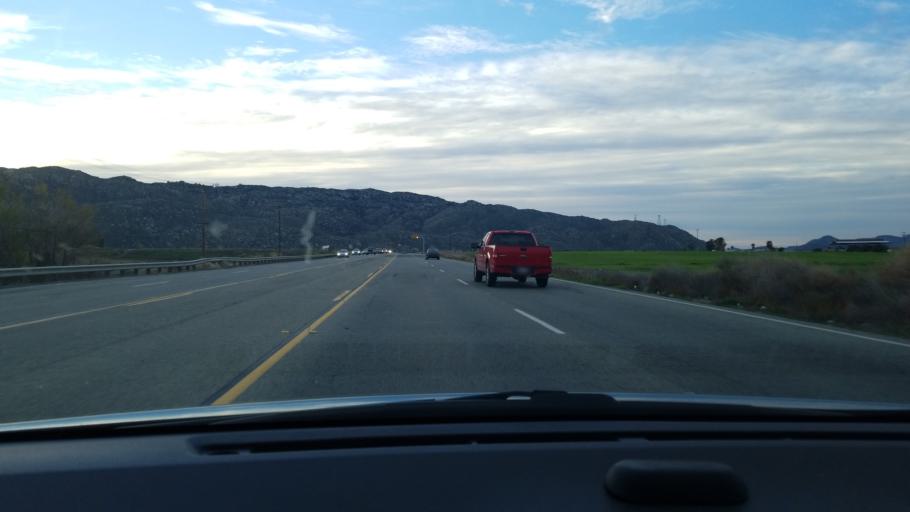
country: US
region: California
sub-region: Riverside County
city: San Jacinto
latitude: 33.8235
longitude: -117.0282
